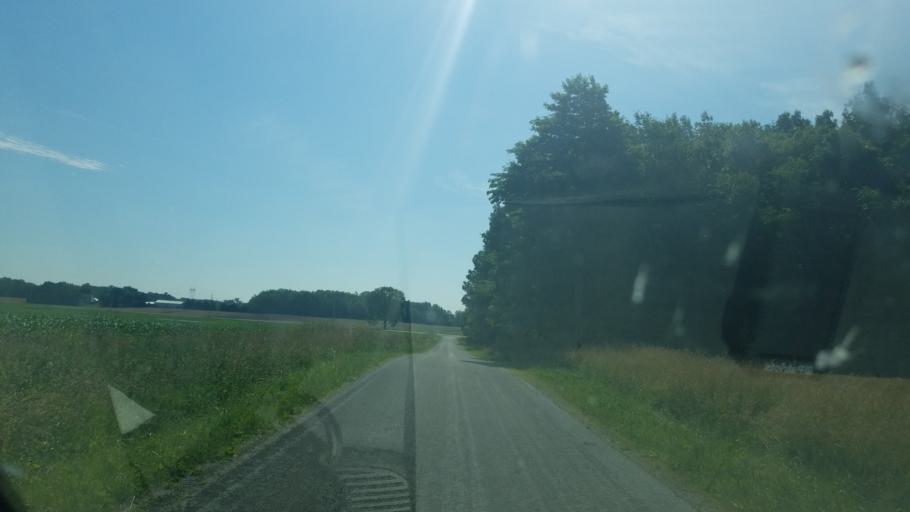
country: US
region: Ohio
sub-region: Wyandot County
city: Carey
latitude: 40.9782
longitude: -83.2729
